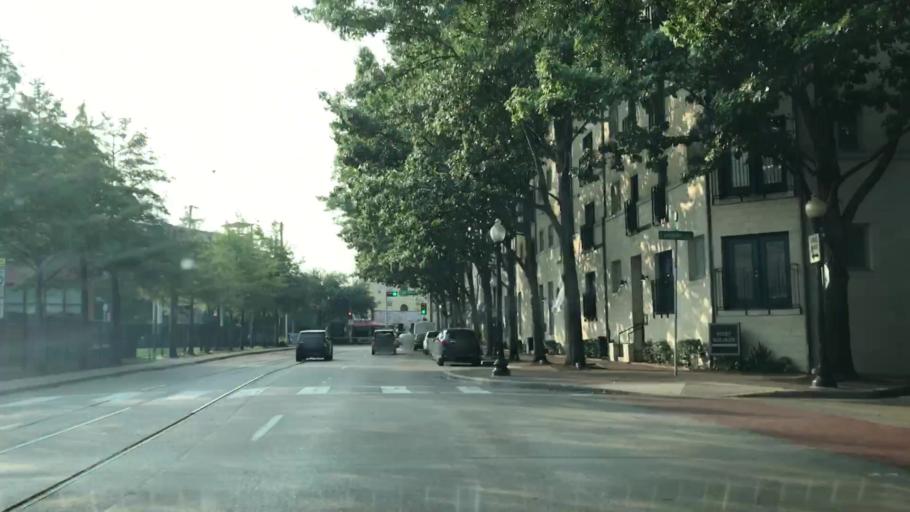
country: US
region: Texas
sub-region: Dallas County
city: Dallas
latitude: 32.8013
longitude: -96.8019
